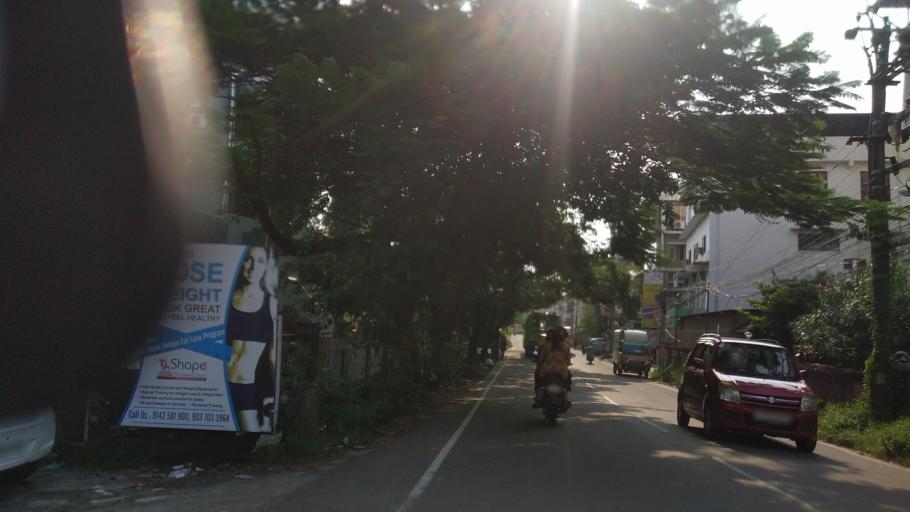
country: IN
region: Kerala
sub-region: Ernakulam
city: Cochin
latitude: 9.9962
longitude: 76.2896
